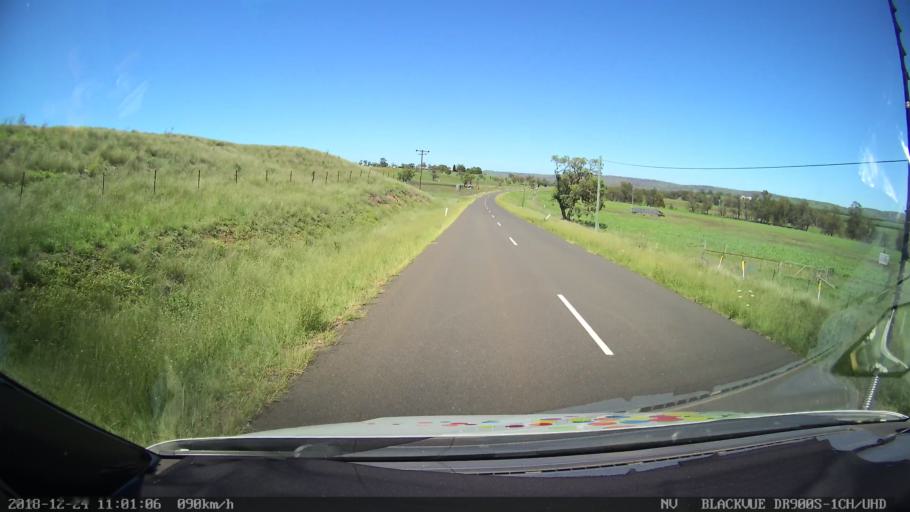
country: AU
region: New South Wales
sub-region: Upper Hunter Shire
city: Merriwa
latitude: -32.0734
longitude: 150.3881
